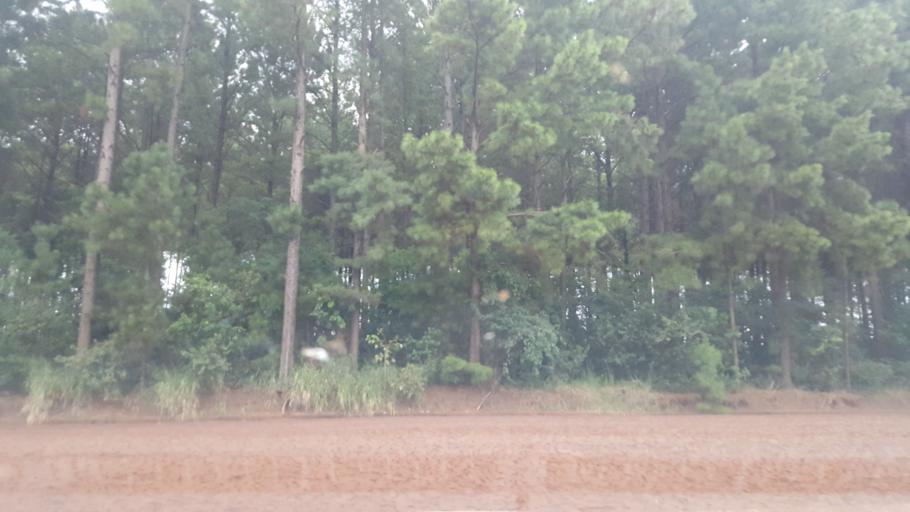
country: AR
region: Misiones
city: Capiovi
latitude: -26.9347
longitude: -55.0440
